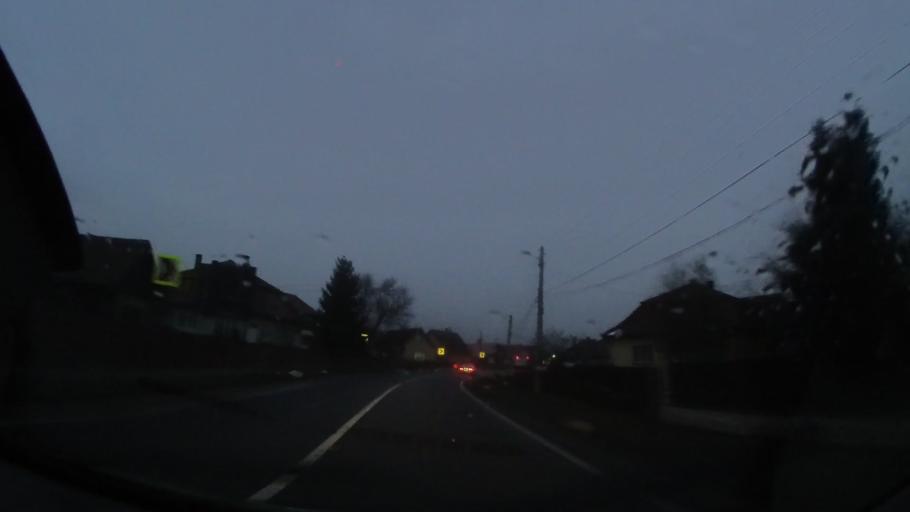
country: RO
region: Harghita
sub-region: Comuna Ditrau
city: Ditrau
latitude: 46.8056
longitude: 25.4940
